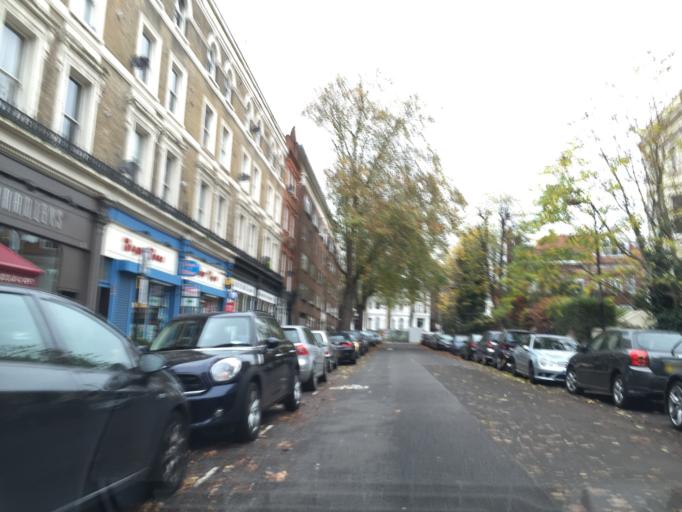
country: GB
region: England
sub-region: Greater London
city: Belsize Park
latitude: 51.5433
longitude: -0.1724
